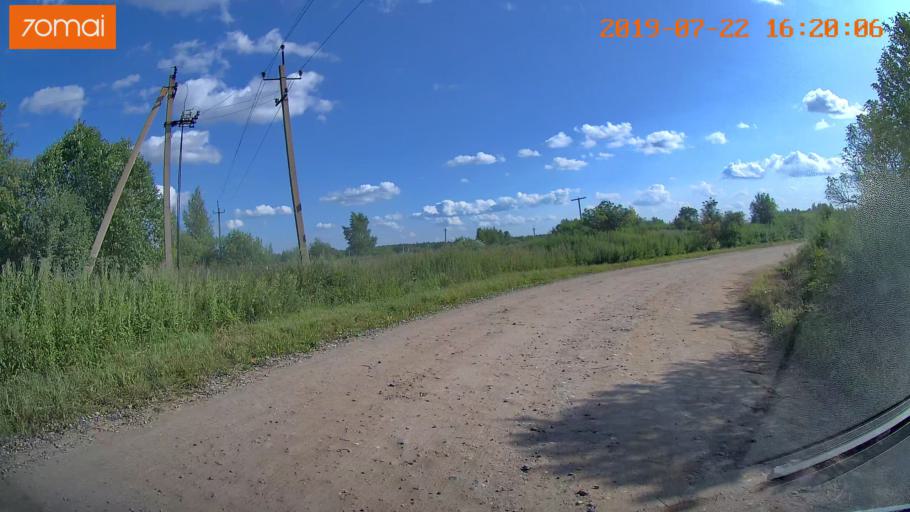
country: RU
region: Ivanovo
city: Novo-Talitsy
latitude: 57.0650
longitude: 40.8935
